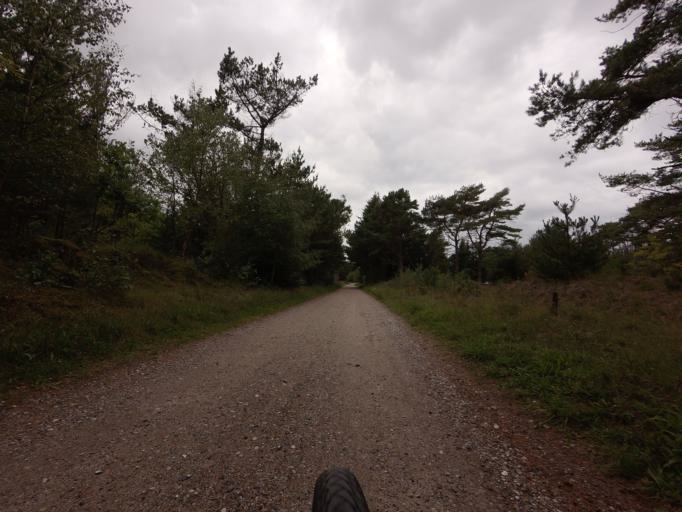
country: DK
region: North Denmark
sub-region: Hjorring Kommune
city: Sindal
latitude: 57.6106
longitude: 10.2819
